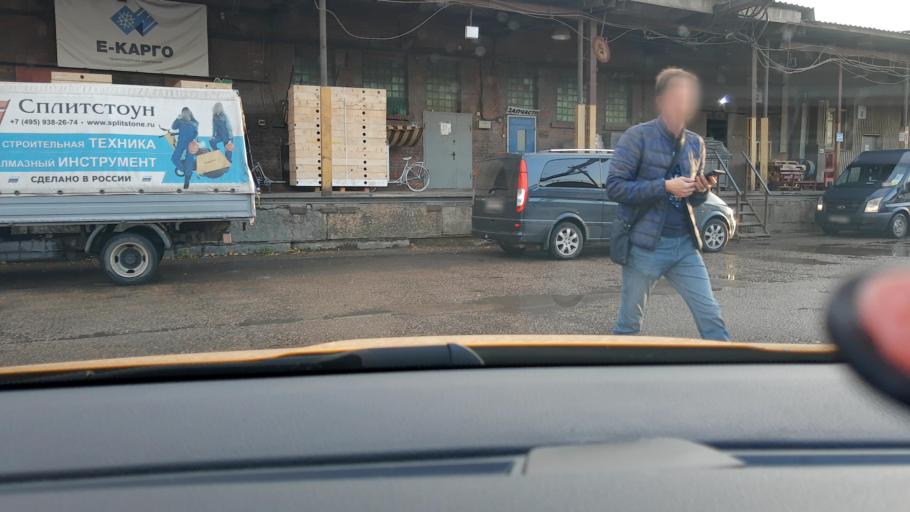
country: RU
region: Moscow
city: Ochakovo-Matveyevskoye
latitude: 55.7045
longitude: 37.4443
